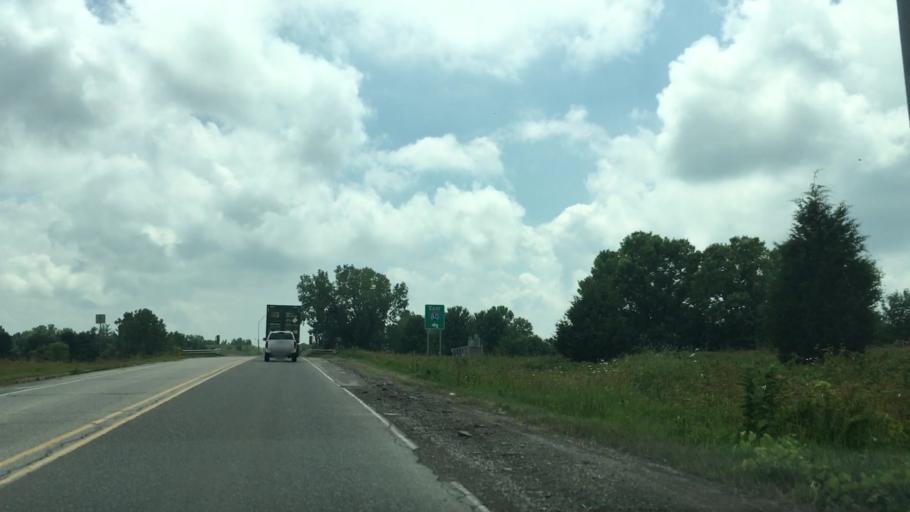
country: US
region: Iowa
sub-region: Johnson County
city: Tiffin
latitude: 41.6951
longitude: -91.6666
